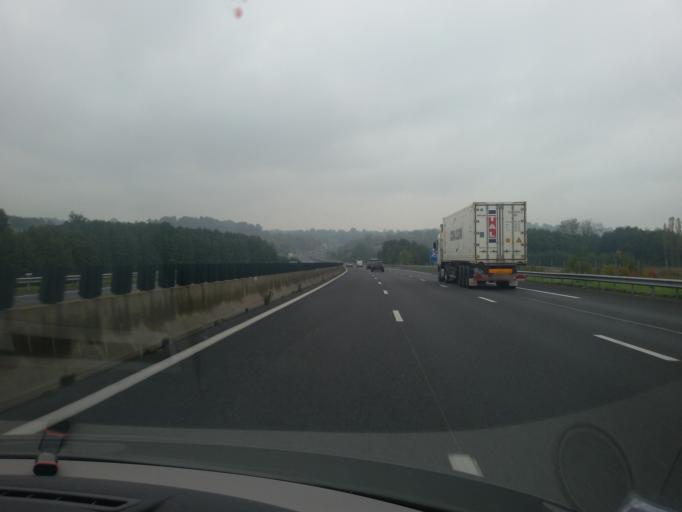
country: FR
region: Haute-Normandie
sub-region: Departement de l'Eure
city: Beuzeville
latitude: 49.3004
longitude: 0.2715
